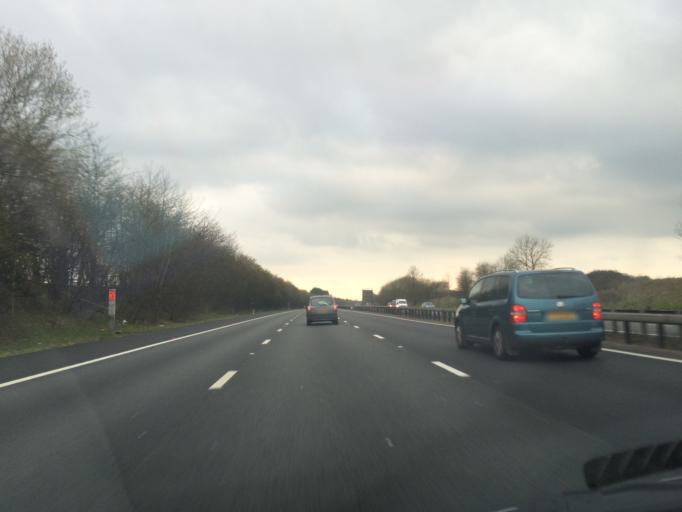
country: GB
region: England
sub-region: West Berkshire
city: Wickham
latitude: 51.4472
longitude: -1.4303
